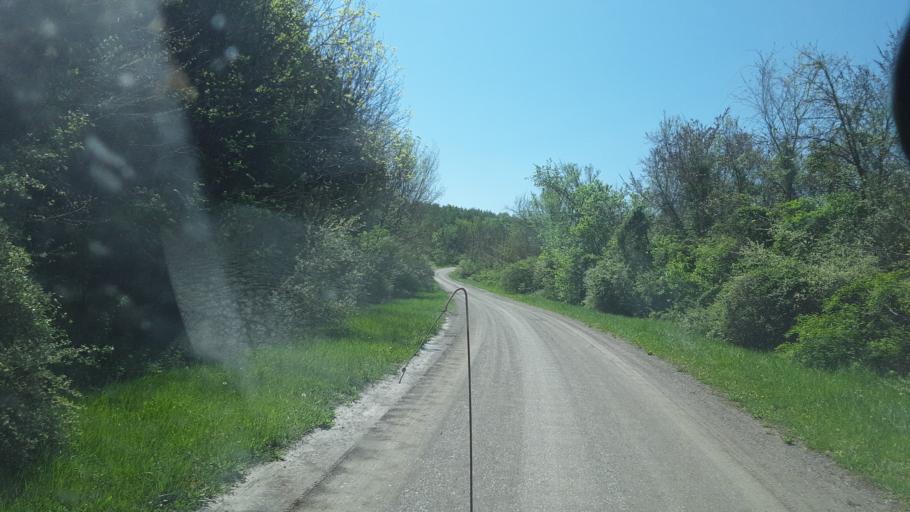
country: US
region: Ohio
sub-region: Noble County
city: Caldwell
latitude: 39.7767
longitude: -81.6186
